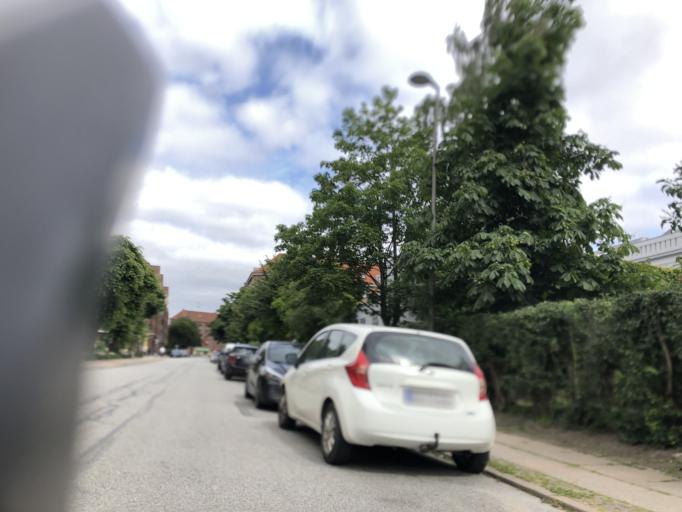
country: DK
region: Capital Region
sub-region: Frederiksberg Kommune
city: Frederiksberg
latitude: 55.6595
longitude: 12.5197
